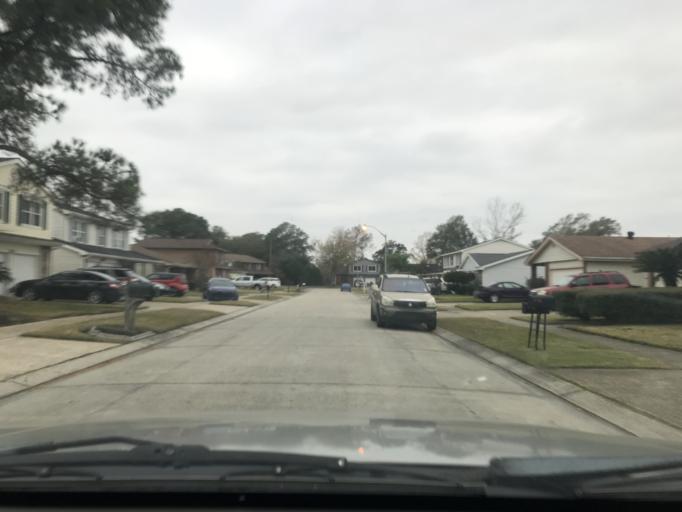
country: US
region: Louisiana
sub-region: Jefferson Parish
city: Woodmere
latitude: 29.8633
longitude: -90.0777
